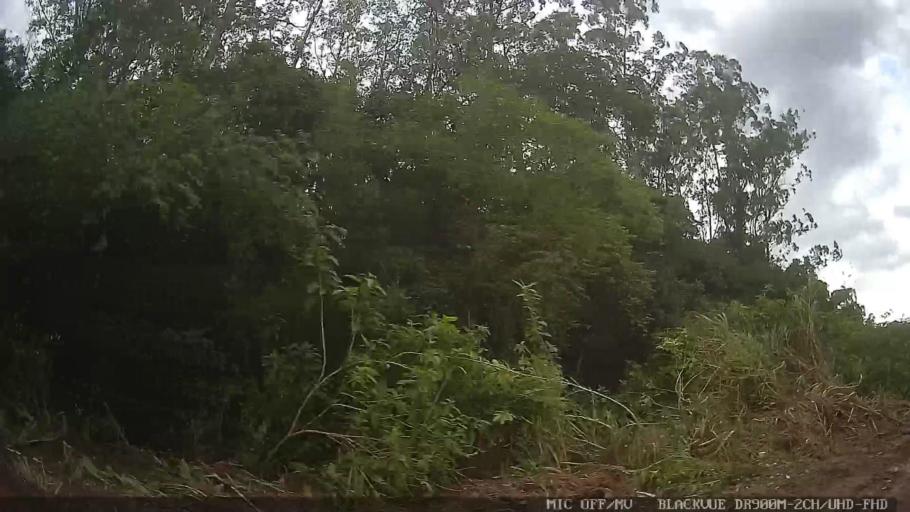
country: BR
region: Sao Paulo
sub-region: Ribeirao Pires
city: Ribeirao Pires
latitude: -23.6948
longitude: -46.4280
